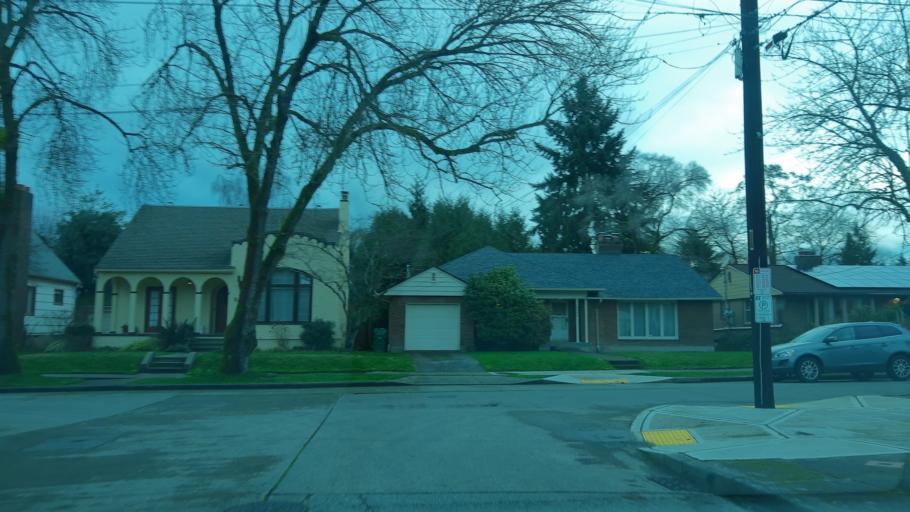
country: US
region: Washington
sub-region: King County
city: Seattle
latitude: 47.6424
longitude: -122.3007
